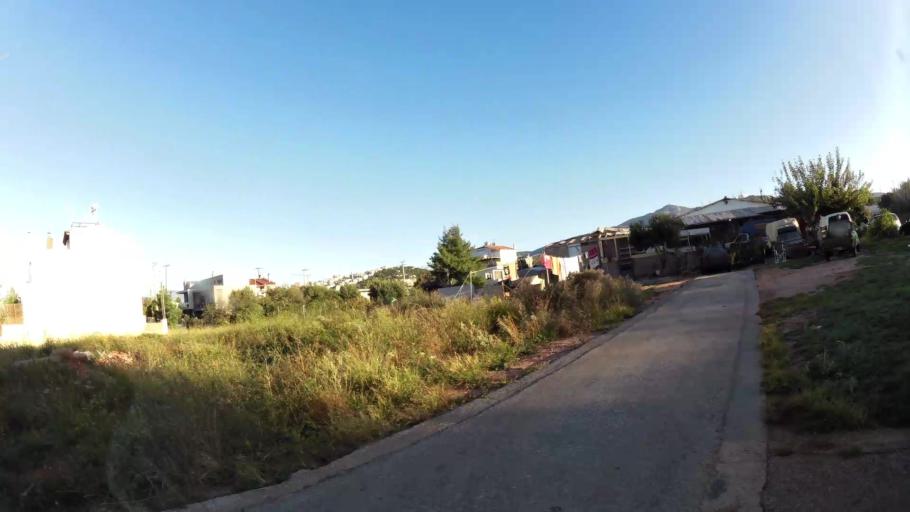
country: GR
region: Attica
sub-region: Nomarchia Anatolikis Attikis
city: Gerakas
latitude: 38.0348
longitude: 23.8525
